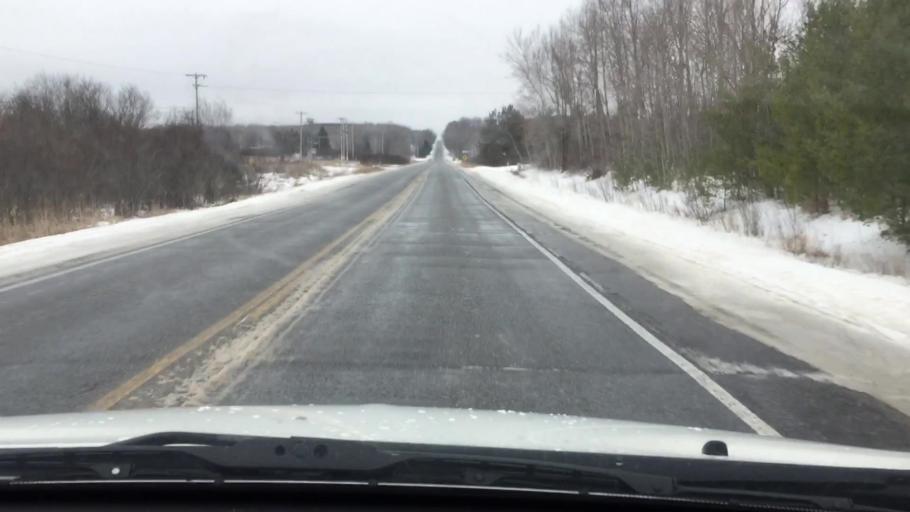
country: US
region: Michigan
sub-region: Wexford County
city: Cadillac
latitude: 44.1070
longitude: -85.4442
